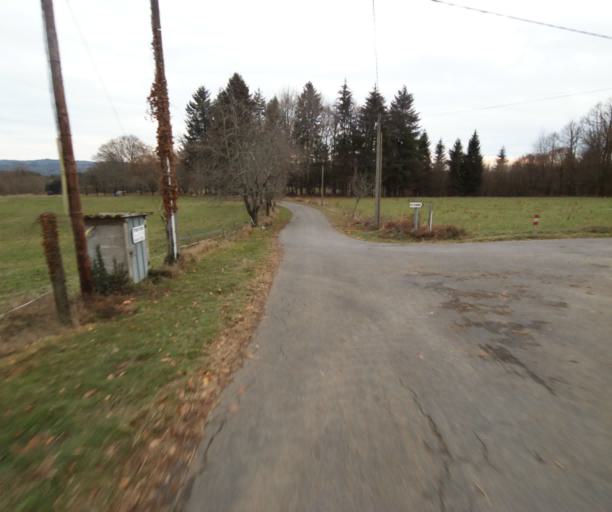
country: FR
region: Limousin
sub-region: Departement de la Correze
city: Chameyrat
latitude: 45.2352
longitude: 1.6696
